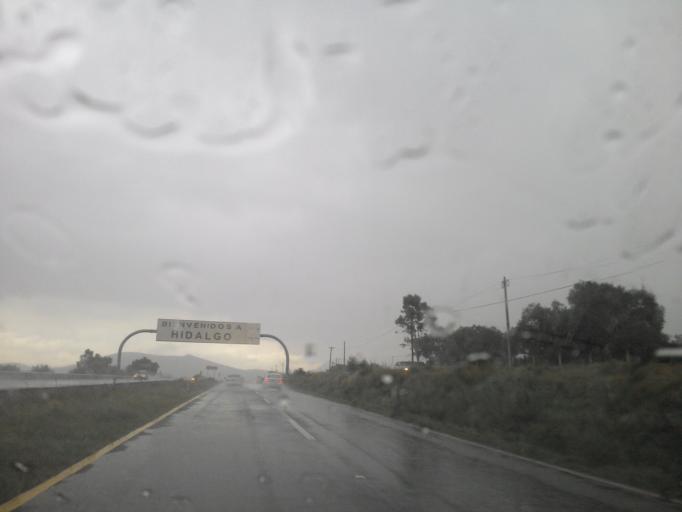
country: MX
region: Hidalgo
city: Zempoala
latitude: 19.8591
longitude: -98.6781
